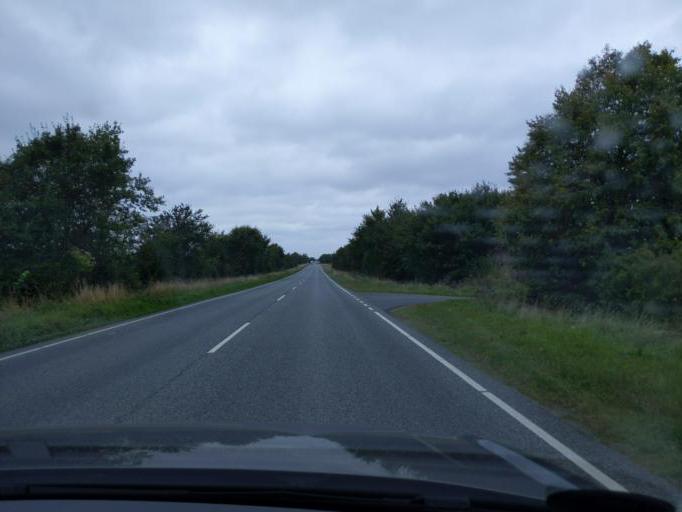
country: DK
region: Central Jutland
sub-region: Randers Kommune
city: Spentrup
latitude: 56.5270
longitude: 9.9242
